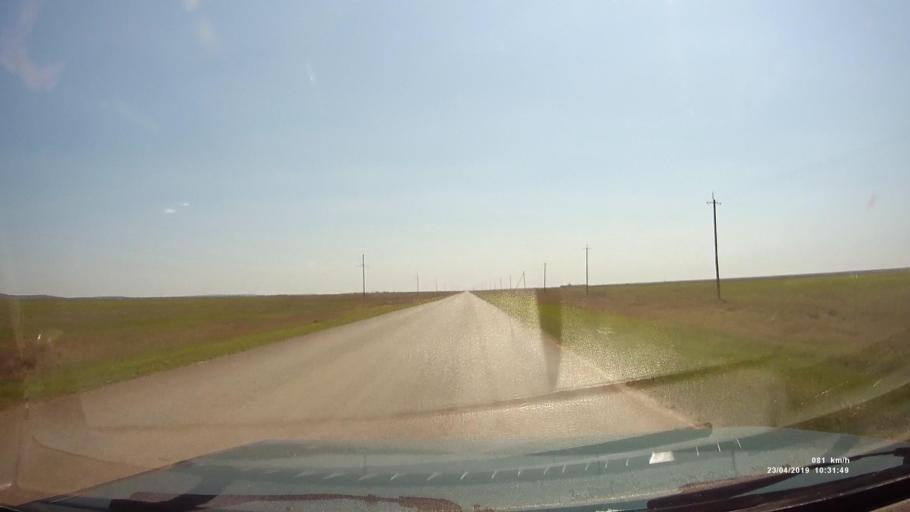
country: RU
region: Kalmykiya
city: Yashalta
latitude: 46.5840
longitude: 42.5673
